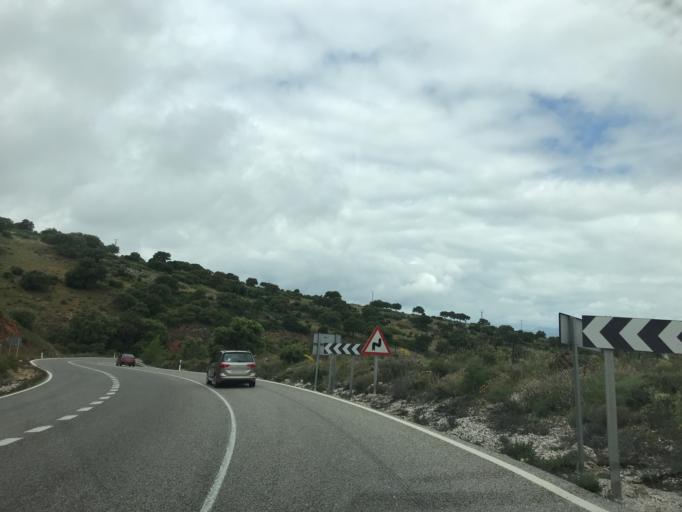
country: ES
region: Andalusia
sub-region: Provincia de Malaga
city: Ronda
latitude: 36.7080
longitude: -5.1306
